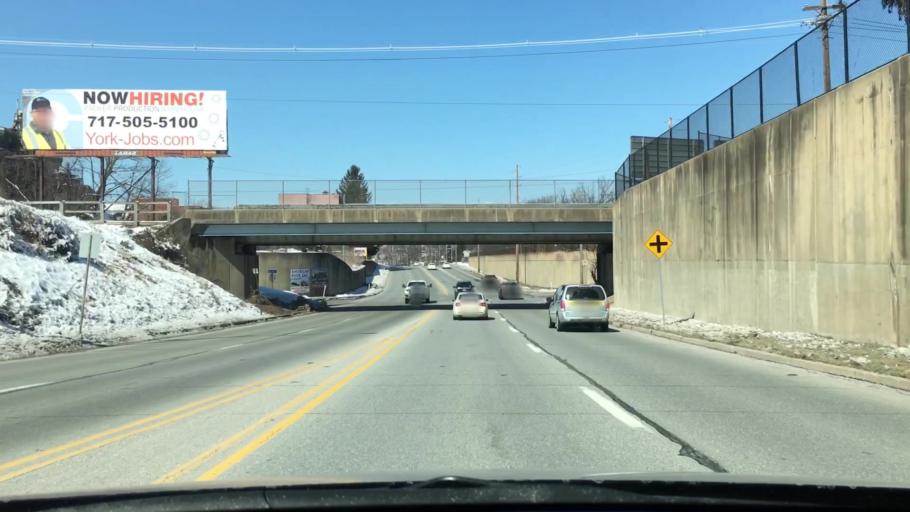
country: US
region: Pennsylvania
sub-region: York County
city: West York
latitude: 39.9448
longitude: -76.7414
